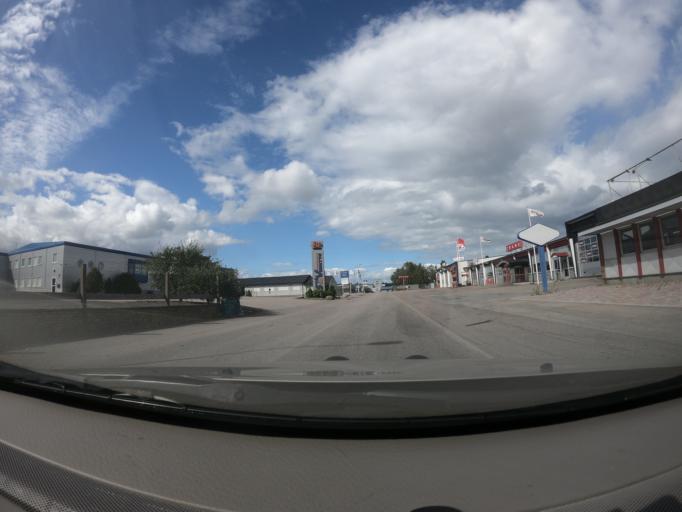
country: SE
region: Kronoberg
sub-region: Vaxjo Kommun
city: Vaexjoe
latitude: 56.8885
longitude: 14.7793
